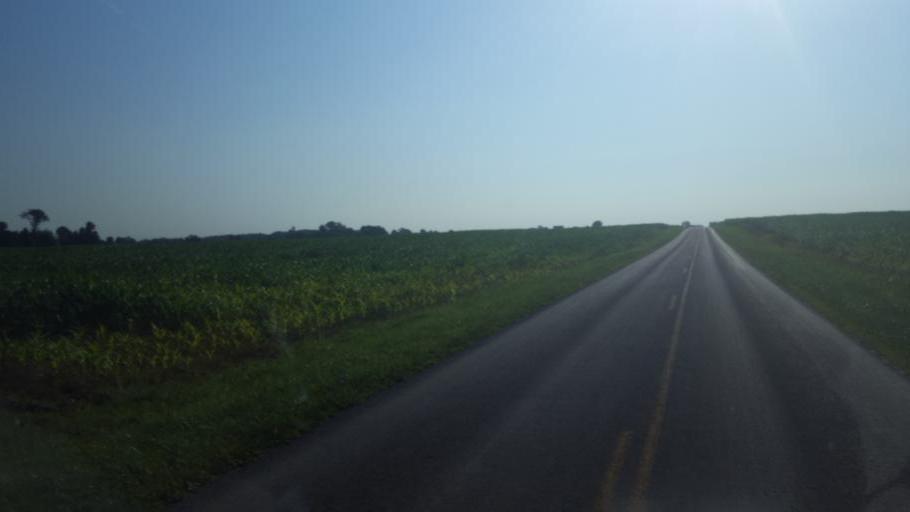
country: US
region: Ohio
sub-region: Hardin County
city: Kenton
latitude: 40.5620
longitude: -83.5545
